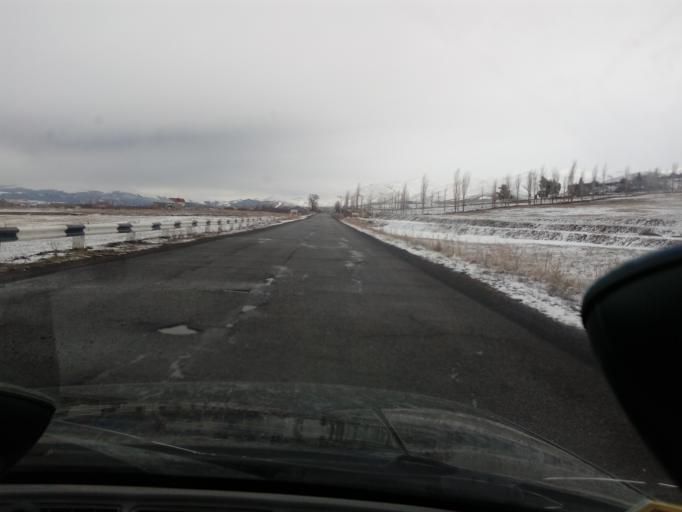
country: AM
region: Geghark'unik'i Marz
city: Geghamavan
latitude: 40.5735
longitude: 44.9032
